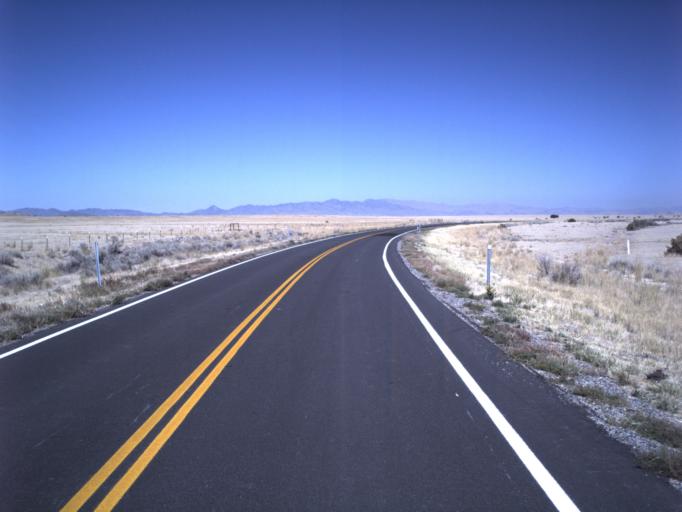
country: US
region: Utah
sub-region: Tooele County
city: Grantsville
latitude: 40.2546
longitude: -112.7388
